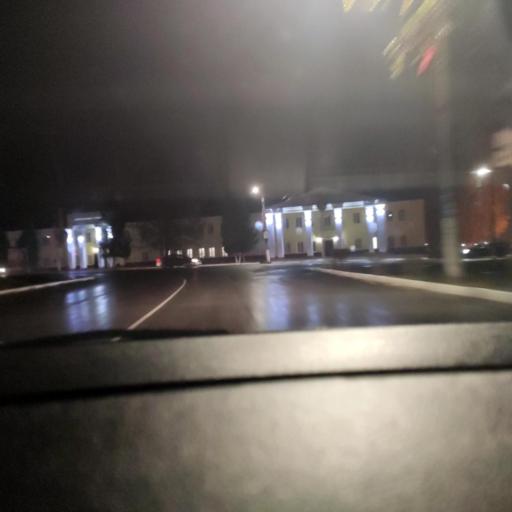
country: RU
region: Voronezj
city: Semiluki
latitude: 51.6868
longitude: 39.0386
